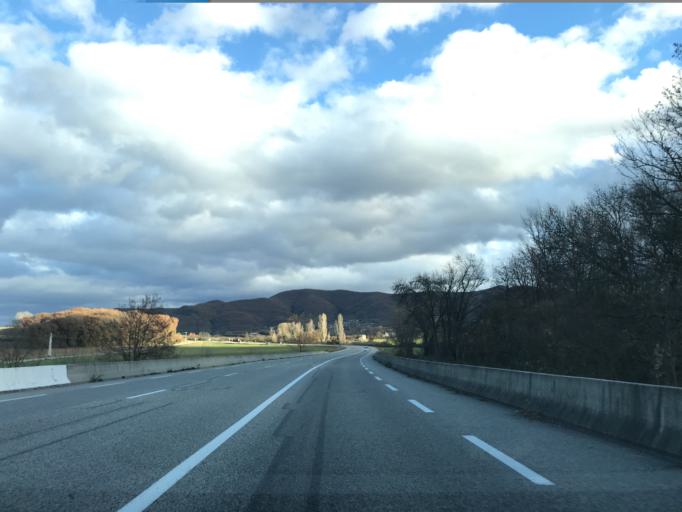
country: FR
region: Rhone-Alpes
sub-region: Departement de l'Ardeche
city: Saint-Julien-en-Saint-Alban
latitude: 44.7108
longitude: 4.7139
